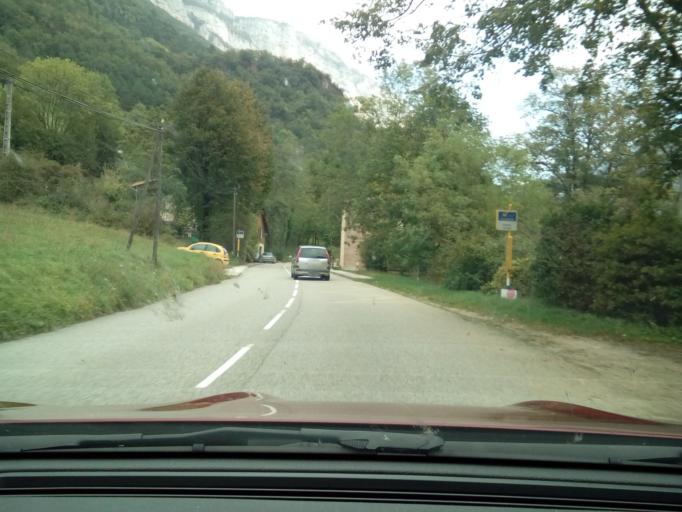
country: FR
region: Rhone-Alpes
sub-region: Departement de l'Isere
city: Pont-en-Royans
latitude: 45.0300
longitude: 5.3841
